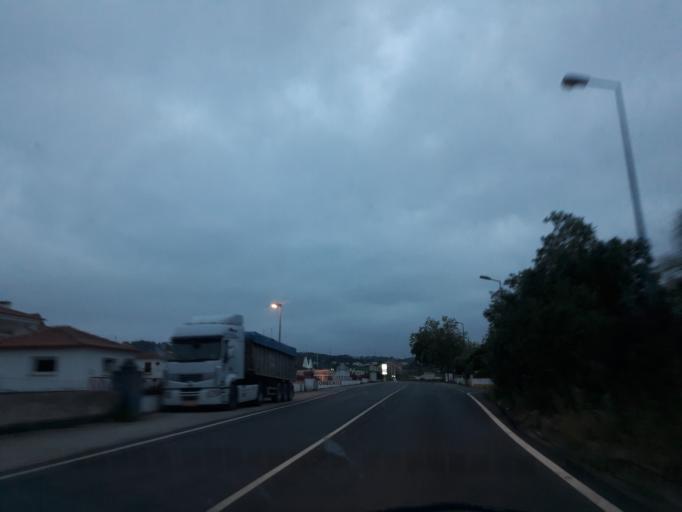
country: PT
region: Leiria
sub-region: Obidos
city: Obidos
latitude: 39.3657
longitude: -9.1486
